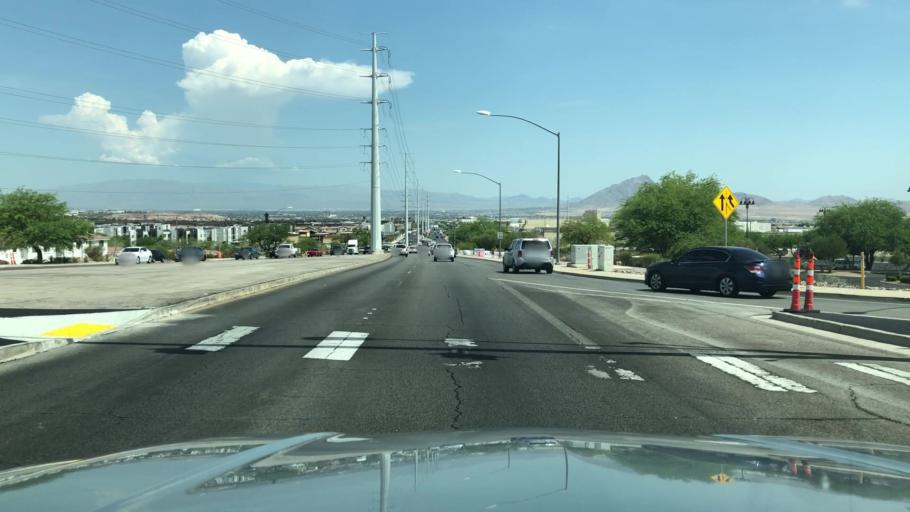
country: US
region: Nevada
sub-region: Clark County
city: Whitney
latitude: 36.0303
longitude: -115.0470
